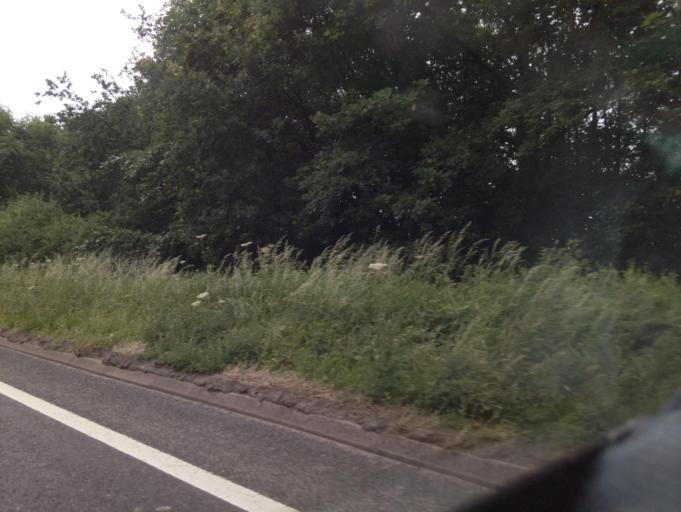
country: GB
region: England
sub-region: Leicestershire
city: Ashby de la Zouch
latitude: 52.7420
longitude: -1.4389
